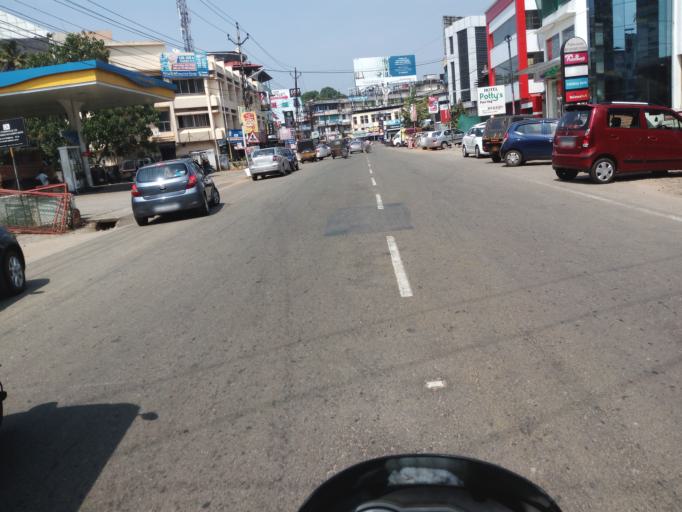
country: IN
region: Kerala
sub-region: Ernakulam
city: Muvattupula
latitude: 9.8998
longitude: 76.7126
